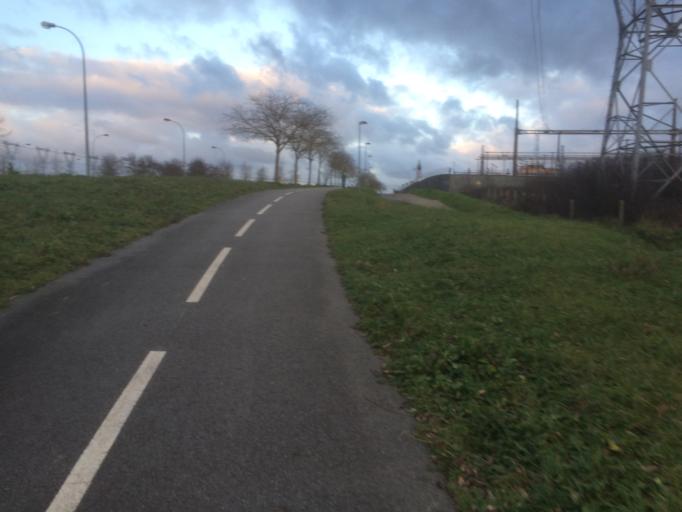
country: FR
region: Ile-de-France
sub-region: Departement de l'Essonne
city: Villejust
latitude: 48.6742
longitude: 2.2262
